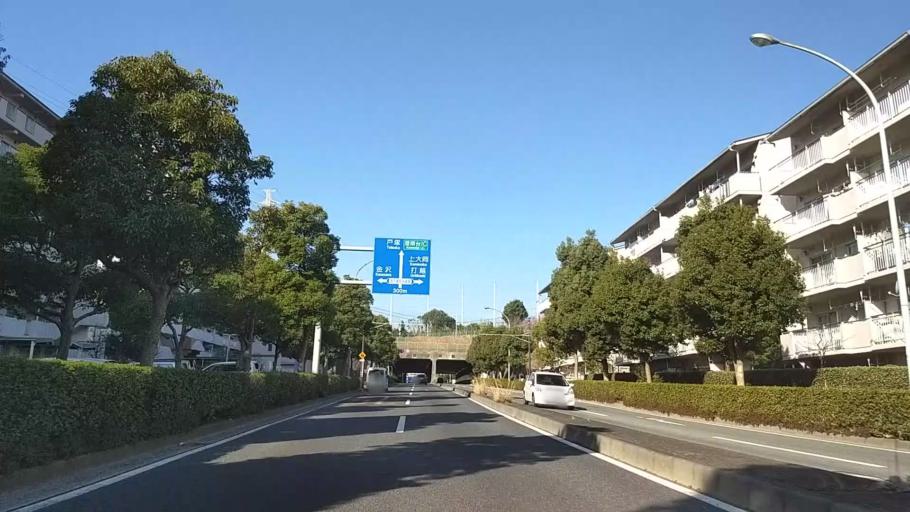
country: JP
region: Kanagawa
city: Yokohama
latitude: 35.3772
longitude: 139.6136
